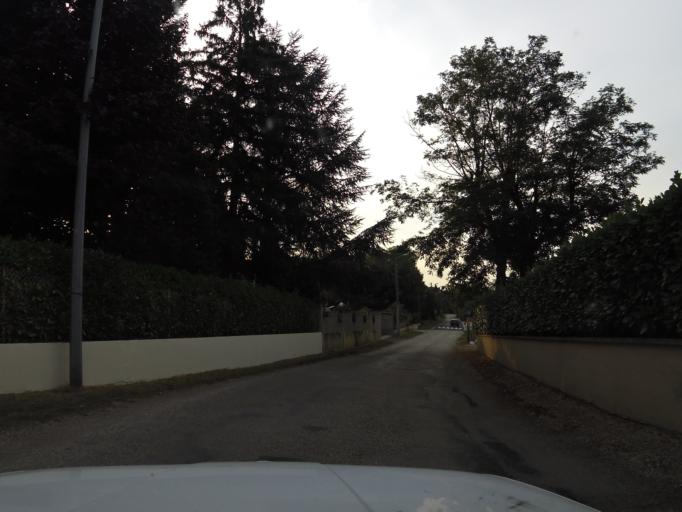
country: FR
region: Rhone-Alpes
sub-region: Departement de l'Ain
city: Saint-Maurice-de-Gourdans
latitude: 45.8257
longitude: 5.1924
